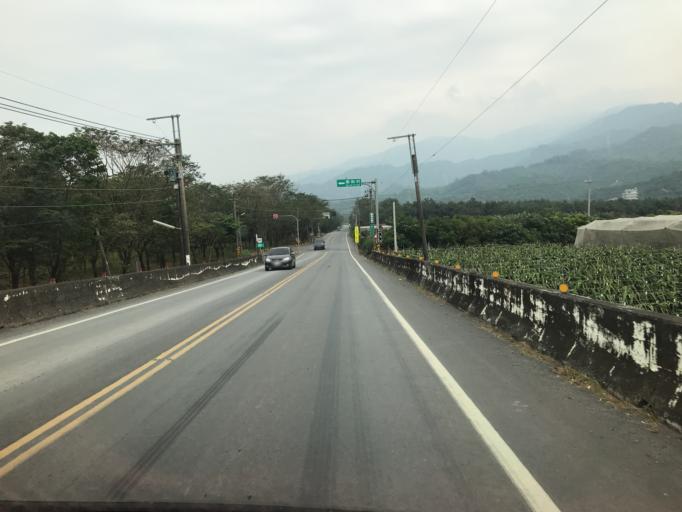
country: TW
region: Taiwan
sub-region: Pingtung
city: Pingtung
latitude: 22.4510
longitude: 120.6091
